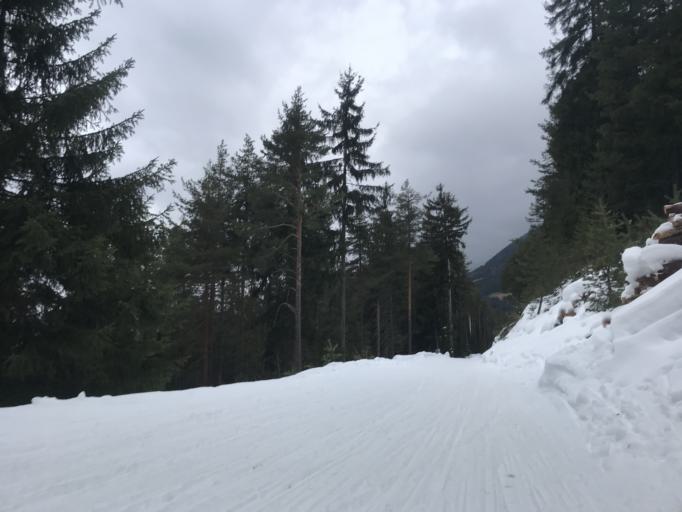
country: IT
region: Trentino-Alto Adige
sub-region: Bolzano
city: Bressanone
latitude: 46.6873
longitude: 11.6846
